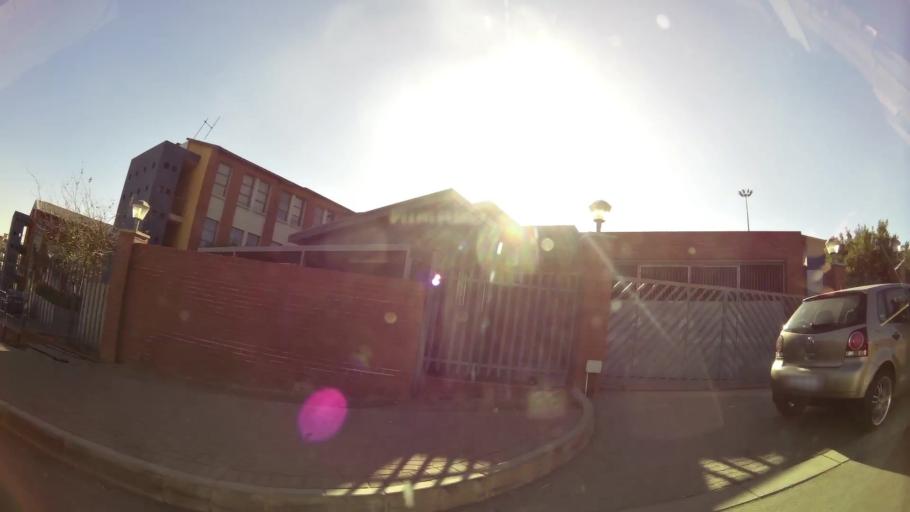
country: ZA
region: Gauteng
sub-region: Ekurhuleni Metropolitan Municipality
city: Tembisa
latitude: -26.0262
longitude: 28.2092
